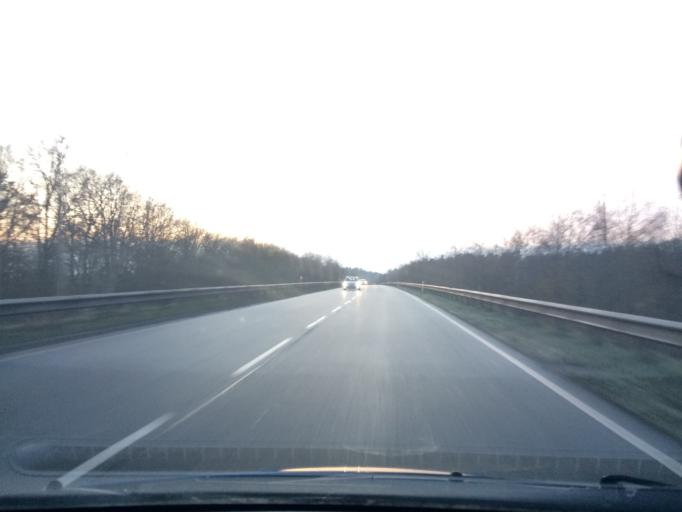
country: DE
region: Lower Saxony
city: Melbeck
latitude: 53.1981
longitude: 10.3821
